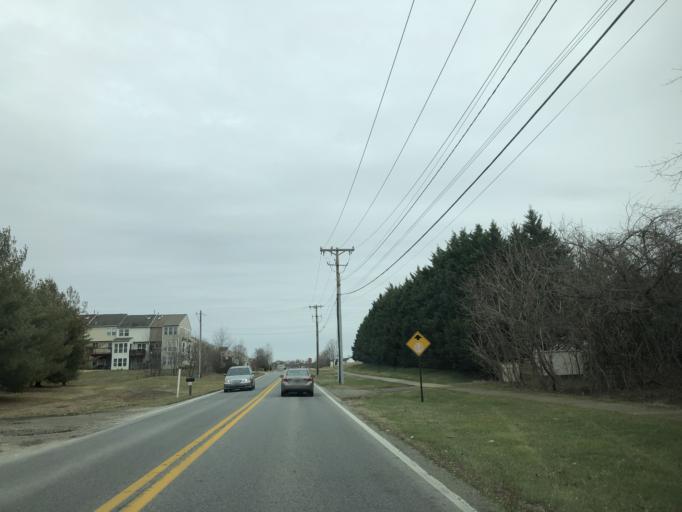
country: US
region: Delaware
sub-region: New Castle County
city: Middletown
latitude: 39.4634
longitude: -75.7161
